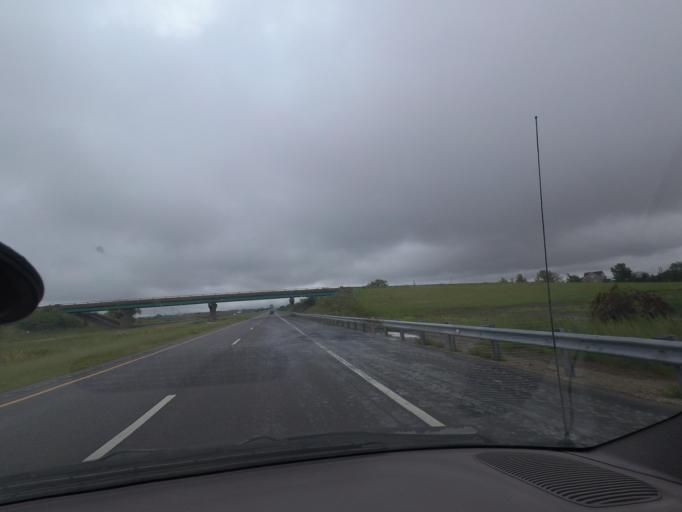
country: US
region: Illinois
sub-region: Champaign County
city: Champaign
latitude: 40.1202
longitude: -88.3348
